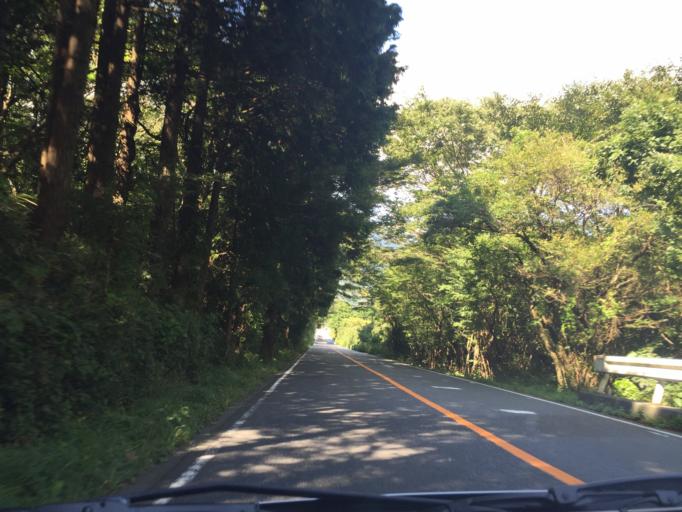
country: JP
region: Kanagawa
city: Hakone
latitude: 35.2556
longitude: 139.0005
